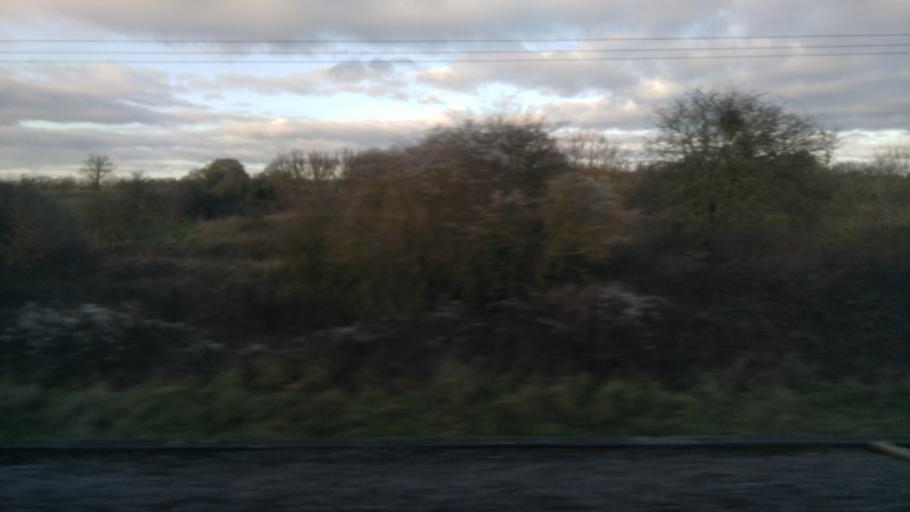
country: GB
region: England
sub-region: Kent
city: Headcorn
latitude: 51.1679
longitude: 0.5992
